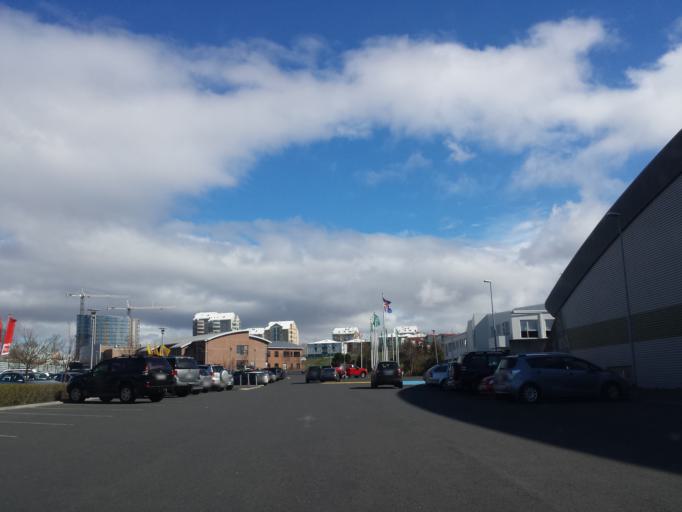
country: IS
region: Capital Region
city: Kopavogur
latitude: 64.1034
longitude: -21.8992
